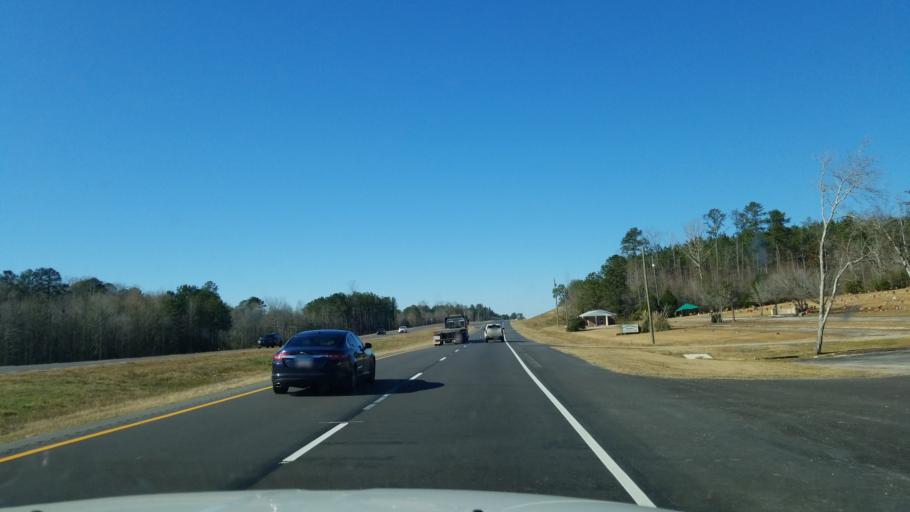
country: US
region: Alabama
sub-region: Pickens County
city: Reform
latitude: 33.3511
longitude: -87.9582
